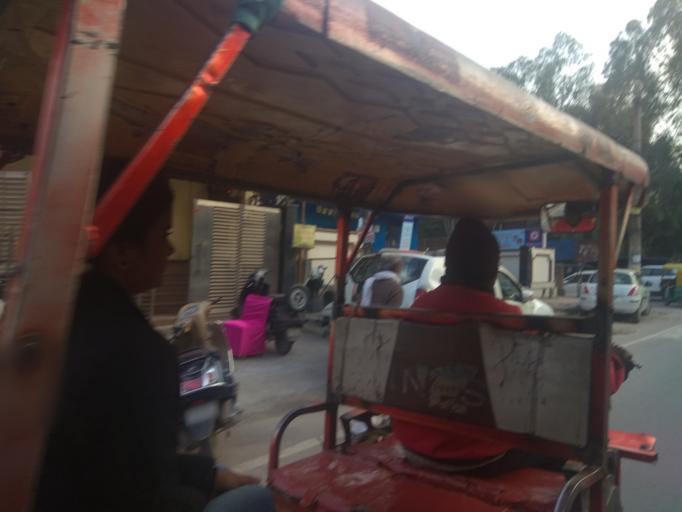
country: IN
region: NCT
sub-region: West Delhi
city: Nangloi Jat
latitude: 28.6321
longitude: 77.0687
